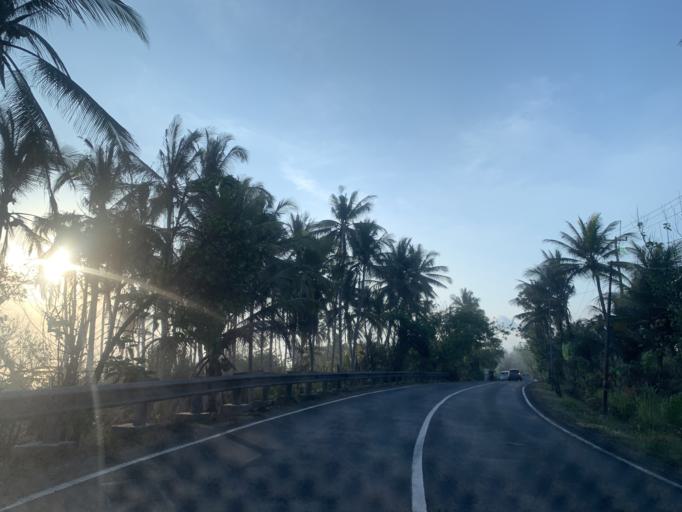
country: ID
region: Bali
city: Banjar Swastika
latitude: -8.4613
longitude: 114.9077
